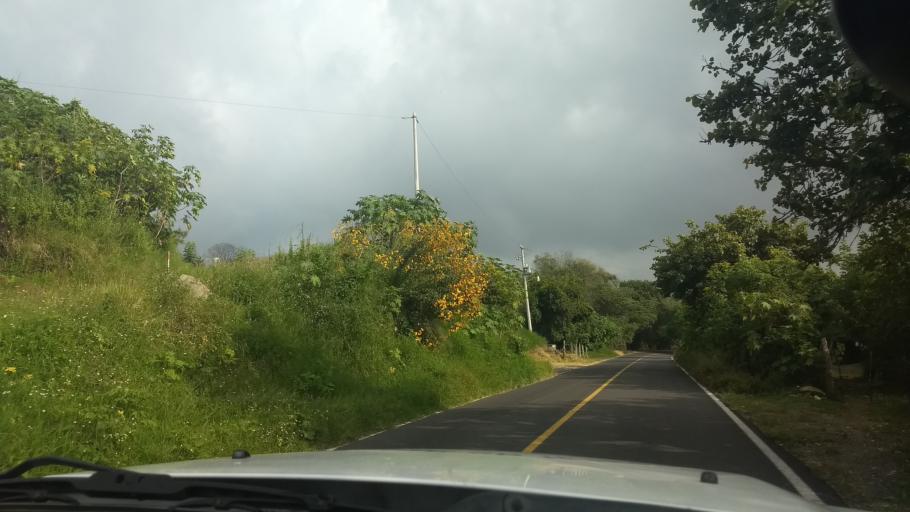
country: MX
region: Colima
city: Queseria
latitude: 19.4044
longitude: -103.6182
